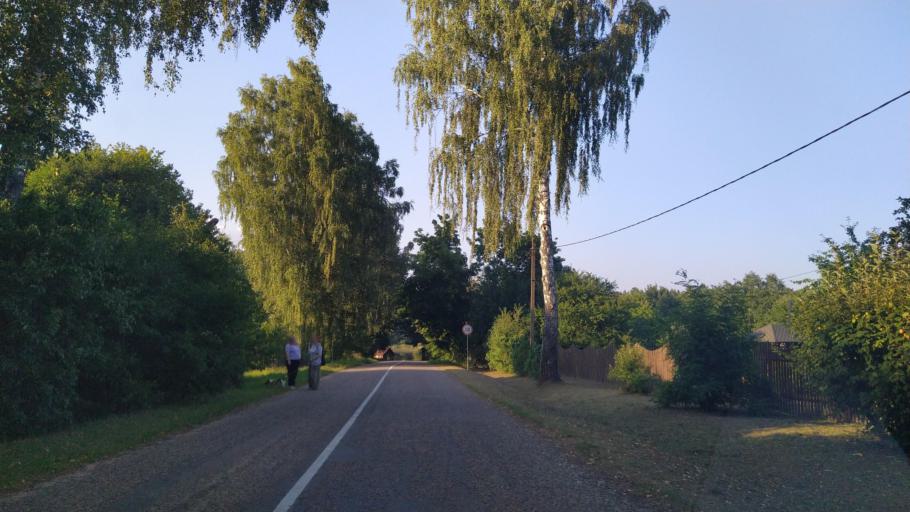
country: RU
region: Pskov
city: Pushkinskiye Gory
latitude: 57.0447
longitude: 28.9171
